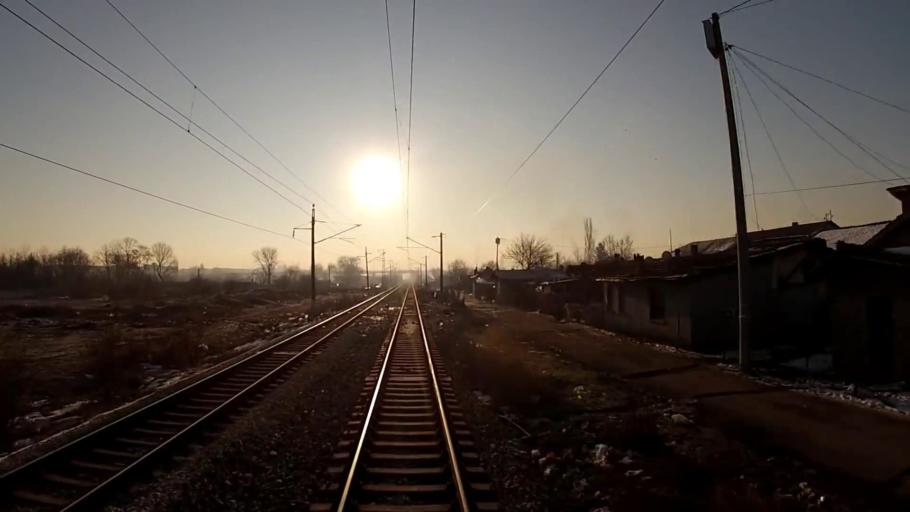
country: BG
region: Sofiya
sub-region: Obshtina Bozhurishte
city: Bozhurishte
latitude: 42.7384
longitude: 23.2640
